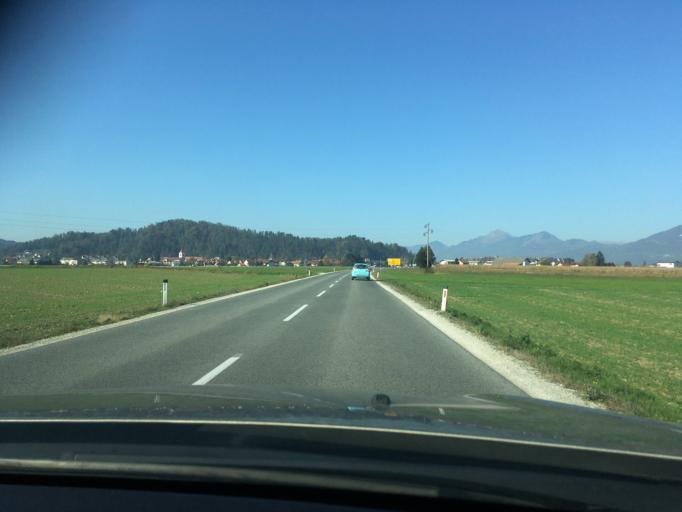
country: SI
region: Menges
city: Menges
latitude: 46.1583
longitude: 14.5829
